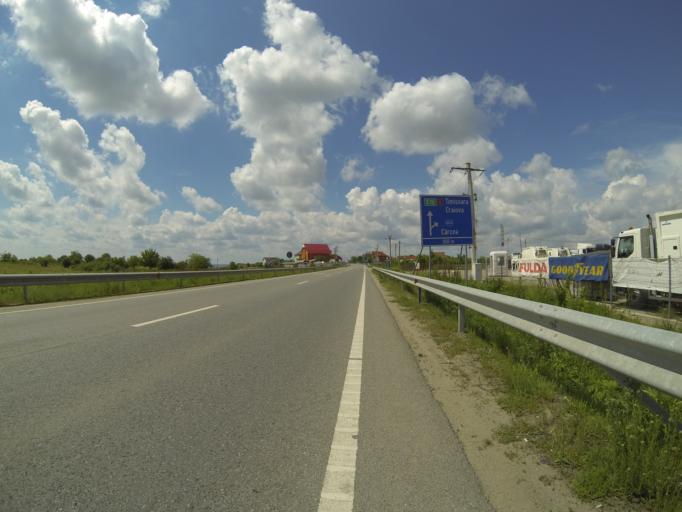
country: RO
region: Dolj
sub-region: Comuna Carcea
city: Carcea
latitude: 44.2623
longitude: 23.9037
